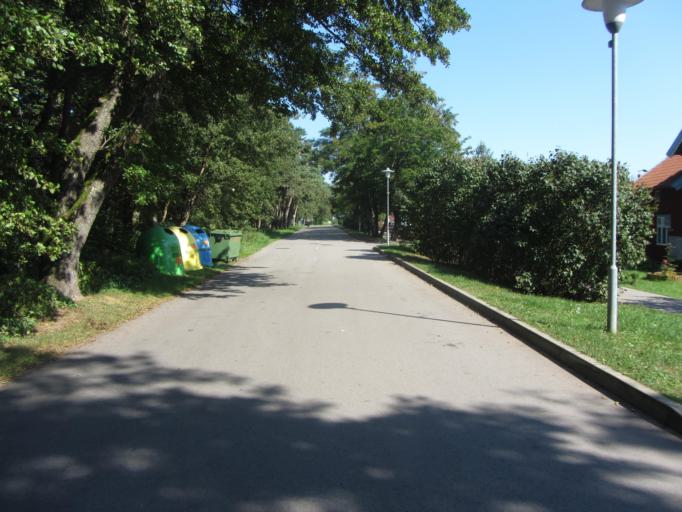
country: LT
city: Neringa
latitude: 55.3720
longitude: 21.0628
